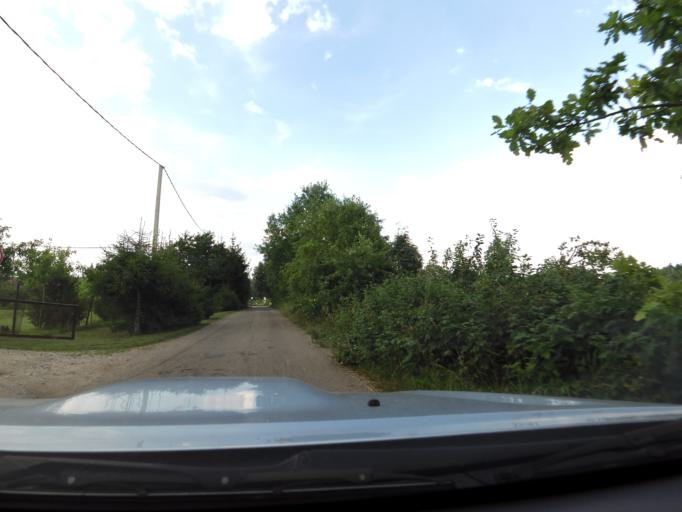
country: LT
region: Siauliu apskritis
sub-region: Siauliai
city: Siauliai
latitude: 55.8655
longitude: 23.1175
